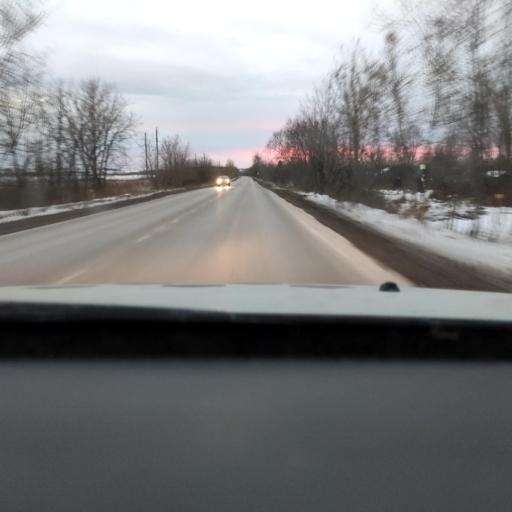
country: RU
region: Perm
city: Kondratovo
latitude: 57.9249
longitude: 56.1105
